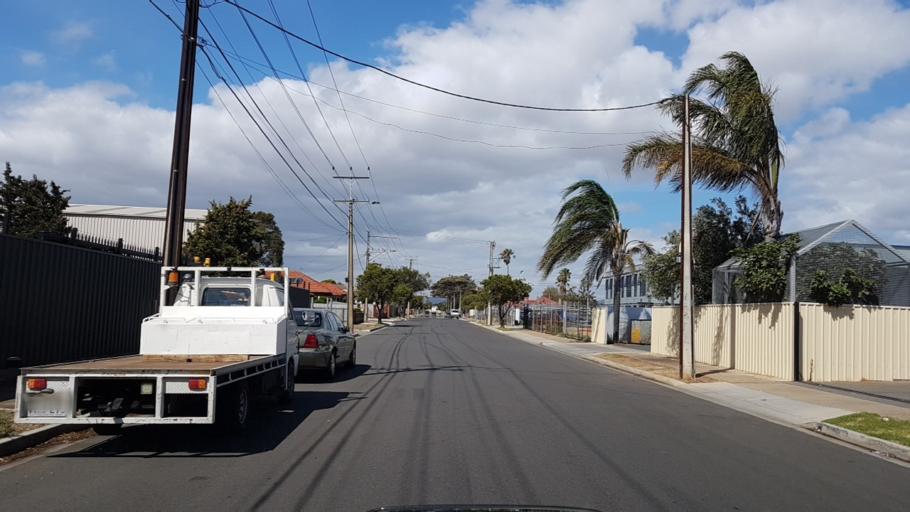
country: AU
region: South Australia
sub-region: Charles Sturt
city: Woodville North
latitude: -34.8527
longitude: 138.5410
